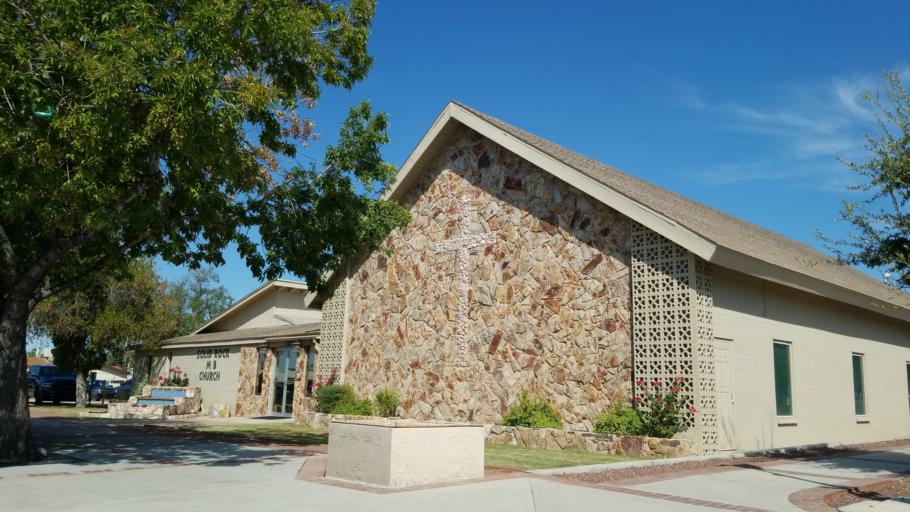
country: US
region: Arizona
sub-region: Maricopa County
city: Peoria
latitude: 33.5805
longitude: -112.2398
